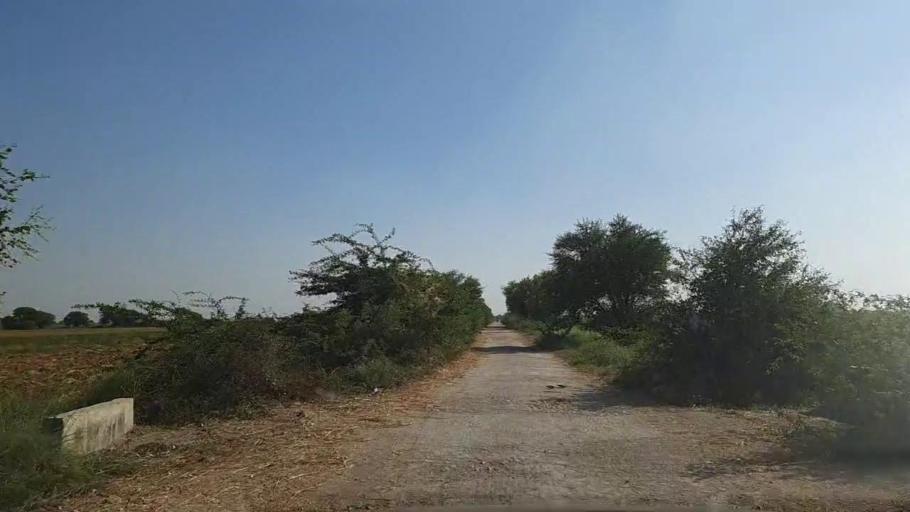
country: PK
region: Sindh
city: Daro Mehar
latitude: 24.7557
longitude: 68.0623
